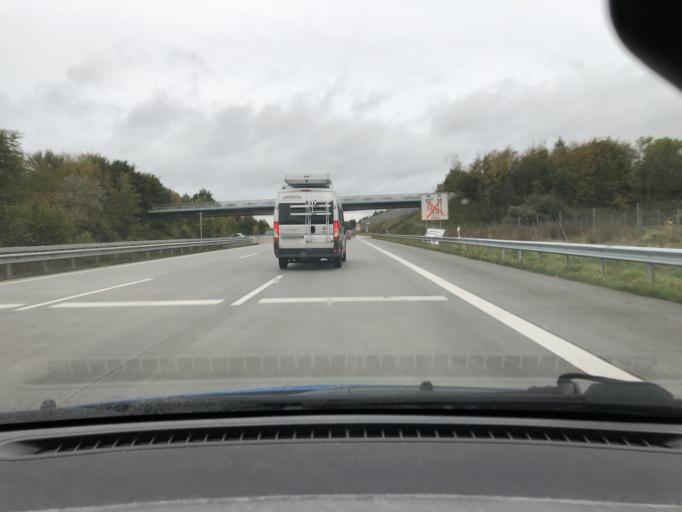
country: DE
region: Schleswig-Holstein
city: Schonbek
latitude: 54.1638
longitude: 9.9629
